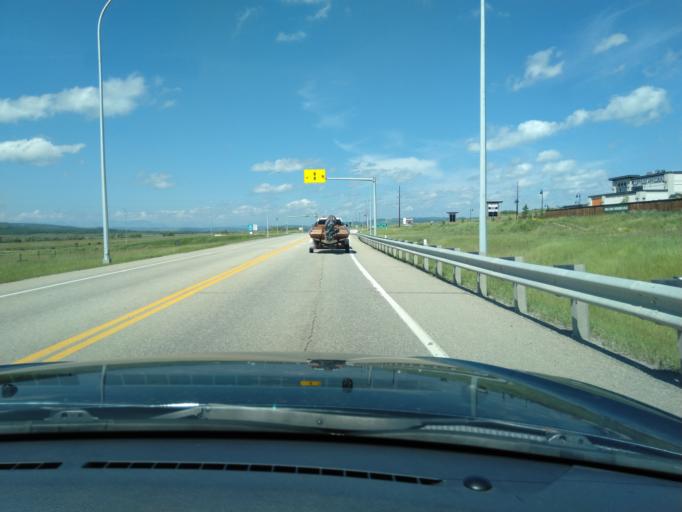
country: CA
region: Alberta
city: Cochrane
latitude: 51.2054
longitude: -114.5096
